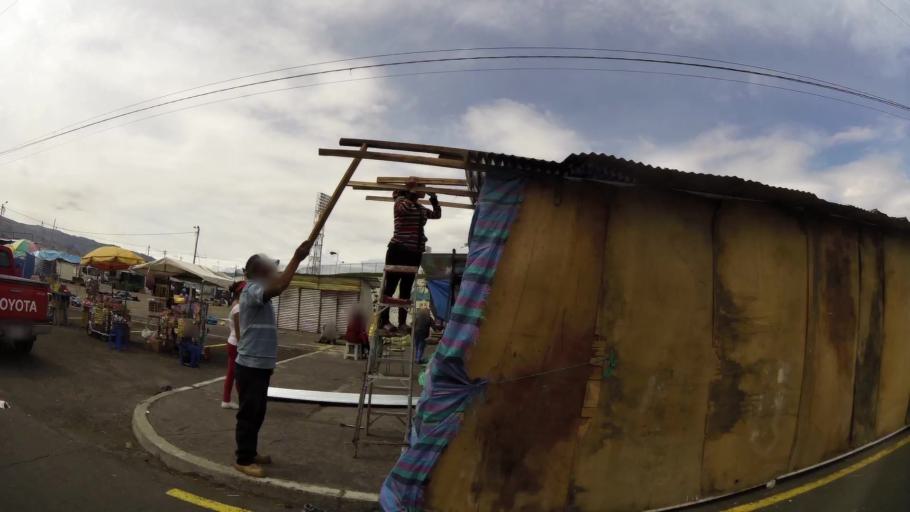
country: EC
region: Cotopaxi
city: Latacunga
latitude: -0.9250
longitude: -78.6147
